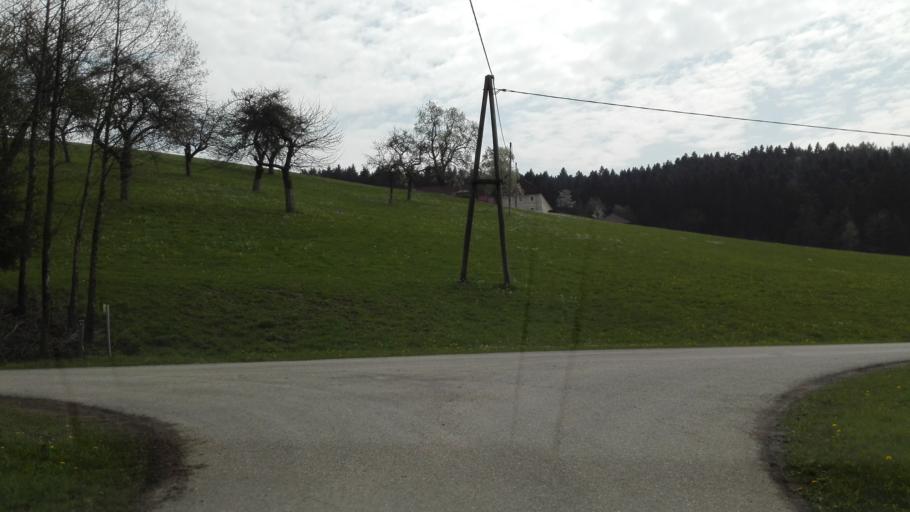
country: AT
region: Upper Austria
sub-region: Politischer Bezirk Perg
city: Perg
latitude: 48.2483
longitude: 14.6934
